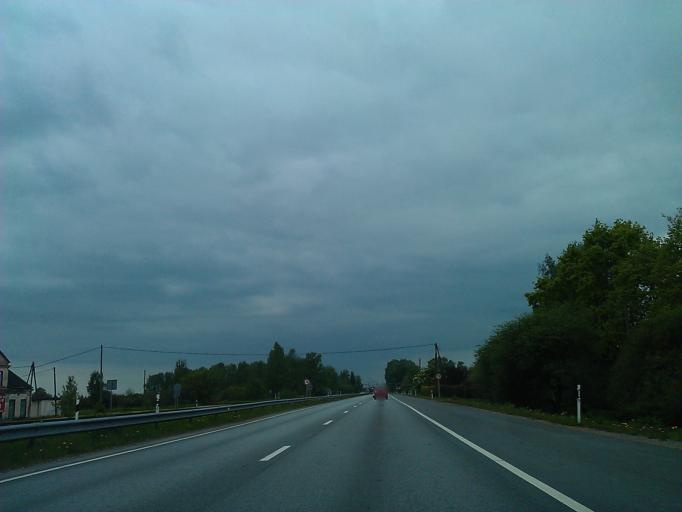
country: LV
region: Olaine
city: Olaine
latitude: 56.7868
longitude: 23.9549
